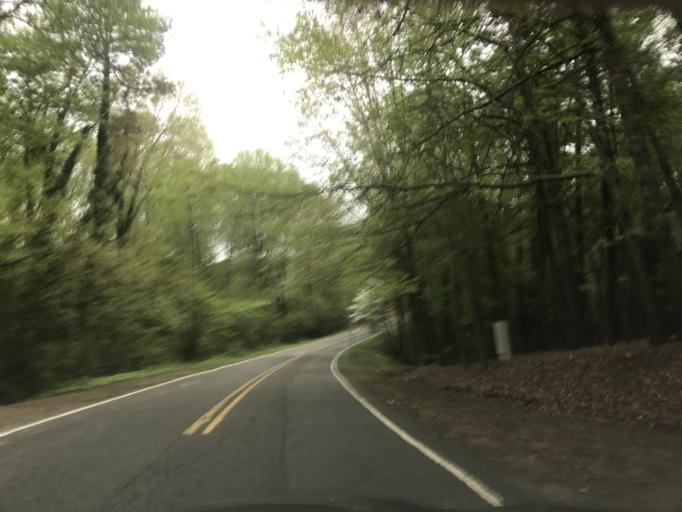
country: US
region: North Carolina
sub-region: Wake County
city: West Raleigh
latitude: 35.7554
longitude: -78.7049
